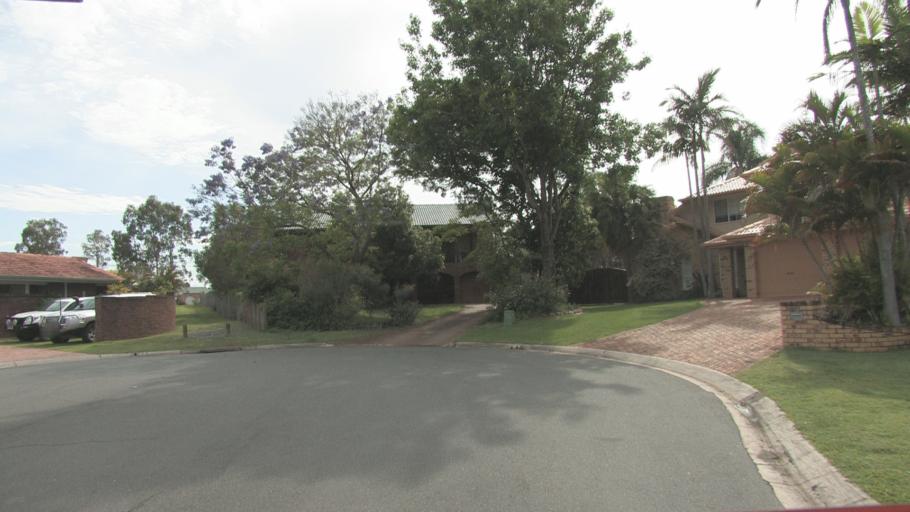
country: AU
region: Queensland
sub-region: Logan
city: Springwood
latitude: -27.6218
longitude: 153.1432
